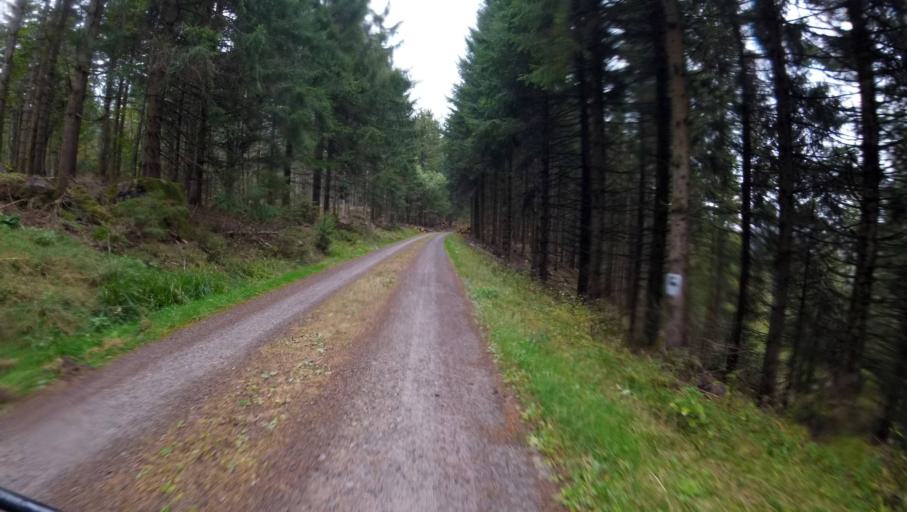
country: DE
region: Baden-Wuerttemberg
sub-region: Karlsruhe Region
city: Enzklosterle
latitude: 48.6661
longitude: 8.4227
